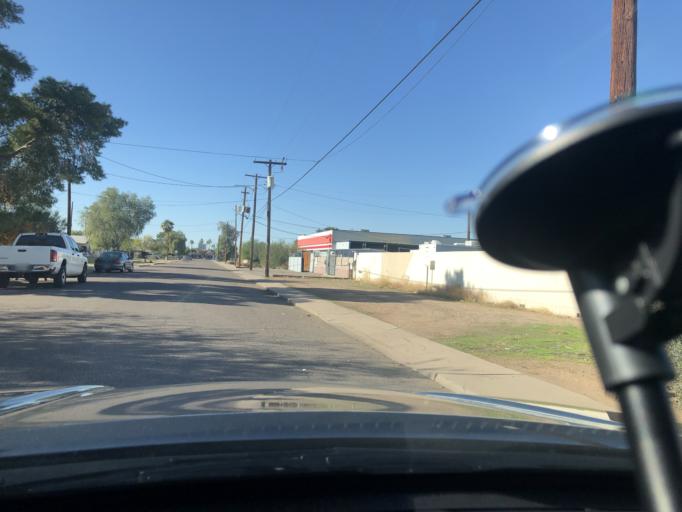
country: US
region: Arizona
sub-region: Maricopa County
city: Phoenix
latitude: 33.4649
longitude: -112.0242
